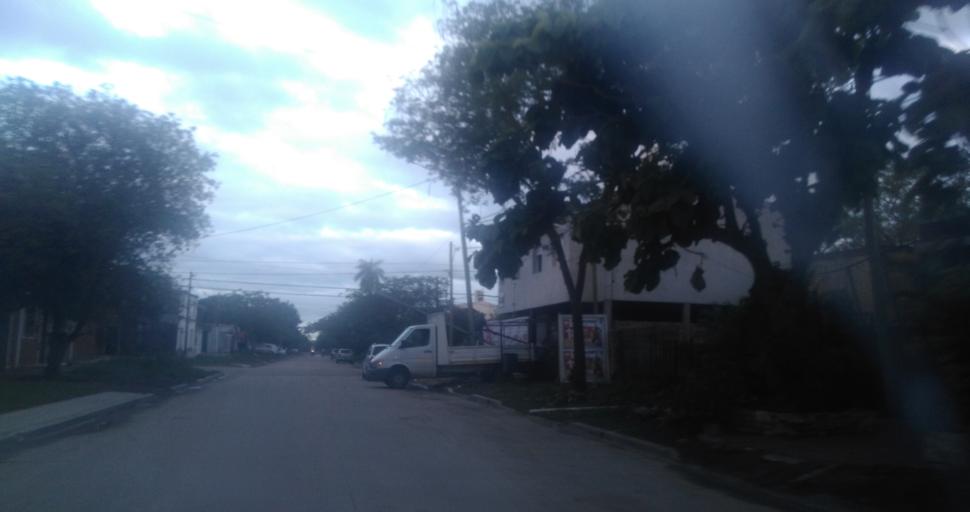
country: AR
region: Chaco
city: Resistencia
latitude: -27.4660
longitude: -58.9688
